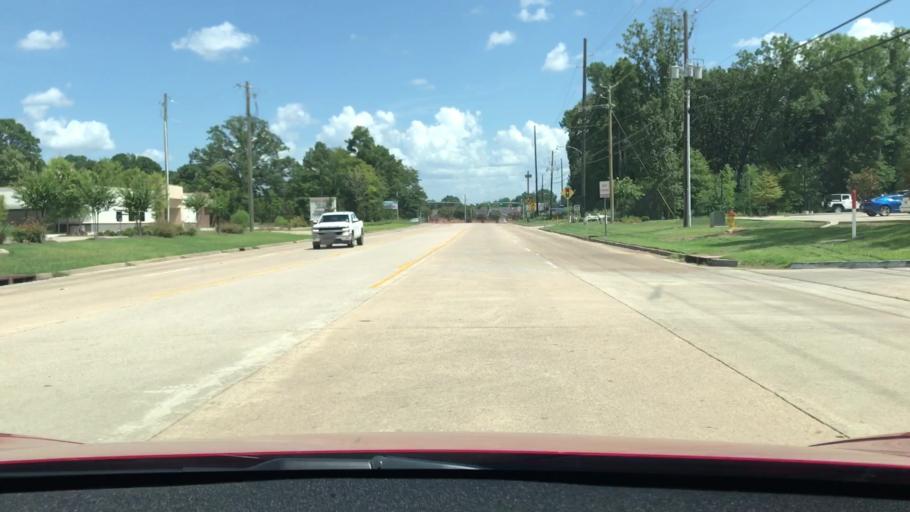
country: US
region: Louisiana
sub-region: Bossier Parish
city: Bossier City
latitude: 32.4231
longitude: -93.7380
